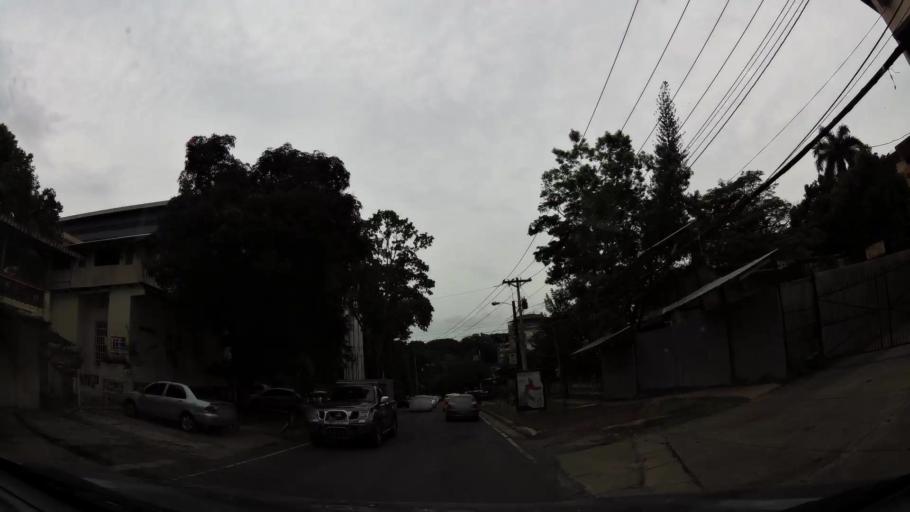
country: PA
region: Panama
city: Panama
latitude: 8.9825
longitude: -79.5323
